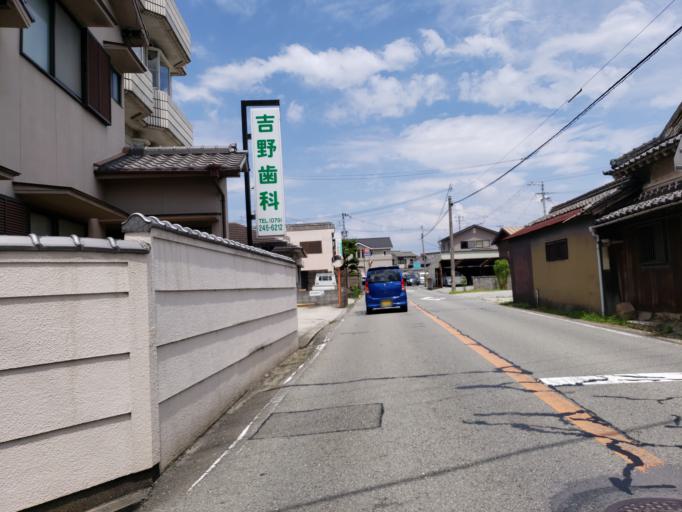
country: JP
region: Hyogo
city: Shirahamacho-usazakiminami
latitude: 34.7884
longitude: 134.6920
